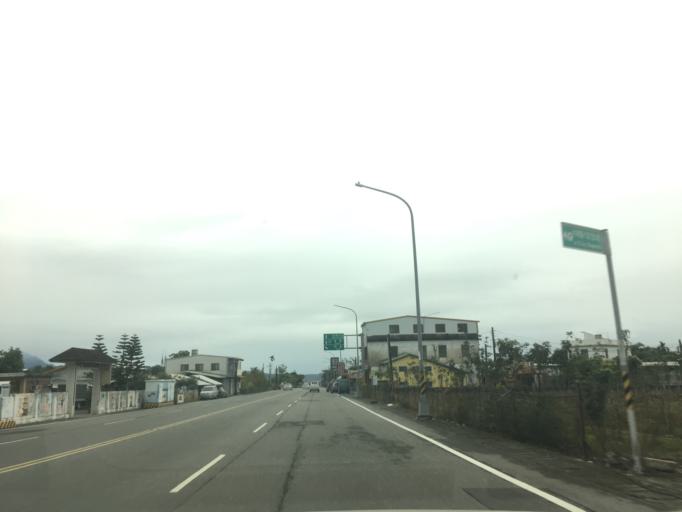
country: TW
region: Taiwan
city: Taitung City
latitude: 22.7636
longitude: 121.0523
